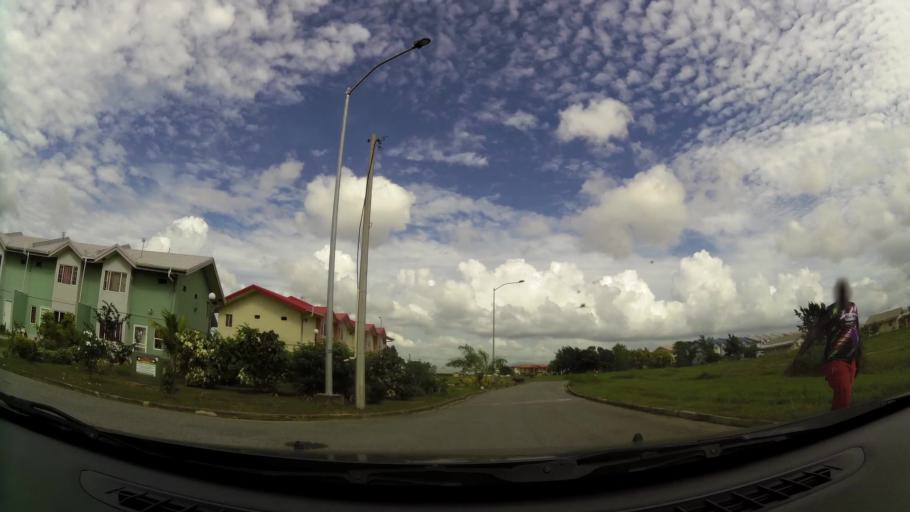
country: TT
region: Chaguanas
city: Chaguanas
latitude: 10.5037
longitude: -61.3960
